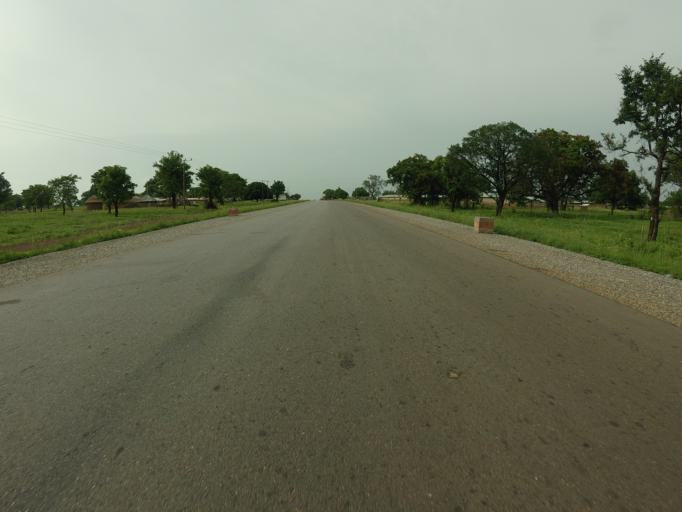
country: GH
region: Northern
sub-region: Yendi
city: Yendi
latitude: 9.6417
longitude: -0.0659
